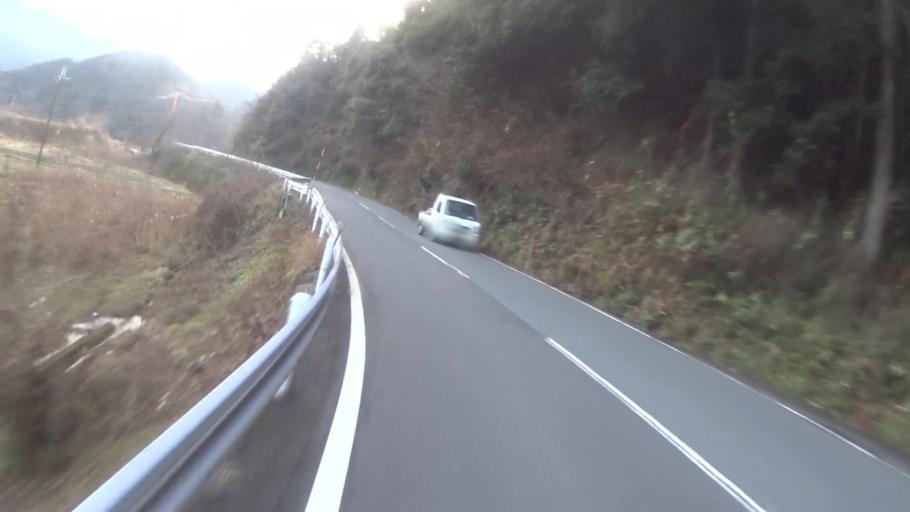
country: JP
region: Kyoto
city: Maizuru
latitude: 35.3694
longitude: 135.4266
